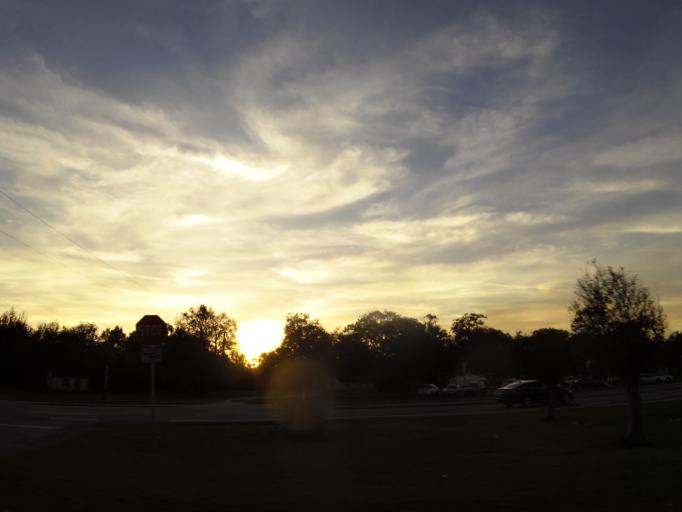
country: US
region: Florida
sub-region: Volusia County
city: North DeLand
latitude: 29.0705
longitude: -81.3047
